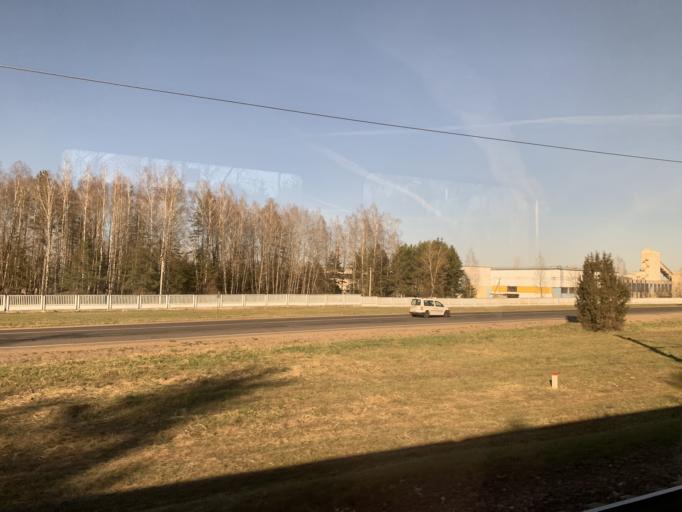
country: BY
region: Grodnenskaya
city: Smarhon'
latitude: 54.4393
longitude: 26.5071
